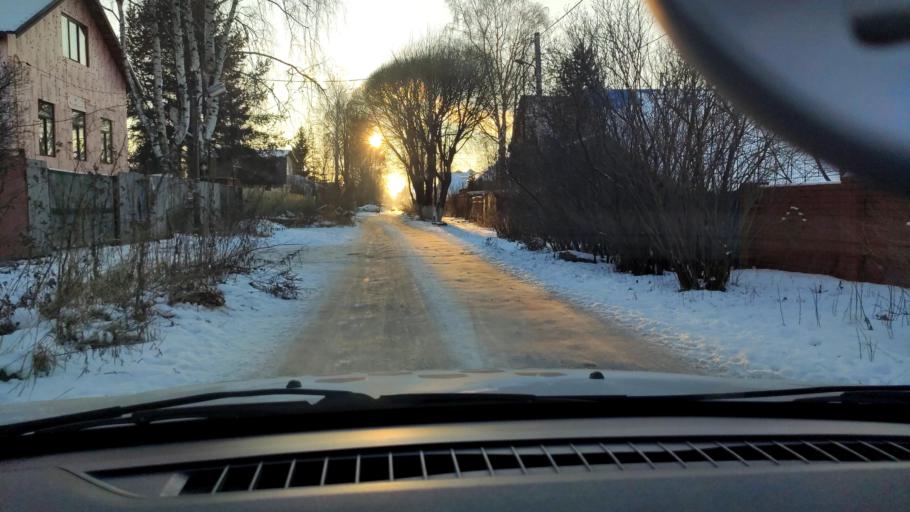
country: RU
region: Perm
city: Perm
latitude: 58.0512
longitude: 56.3309
